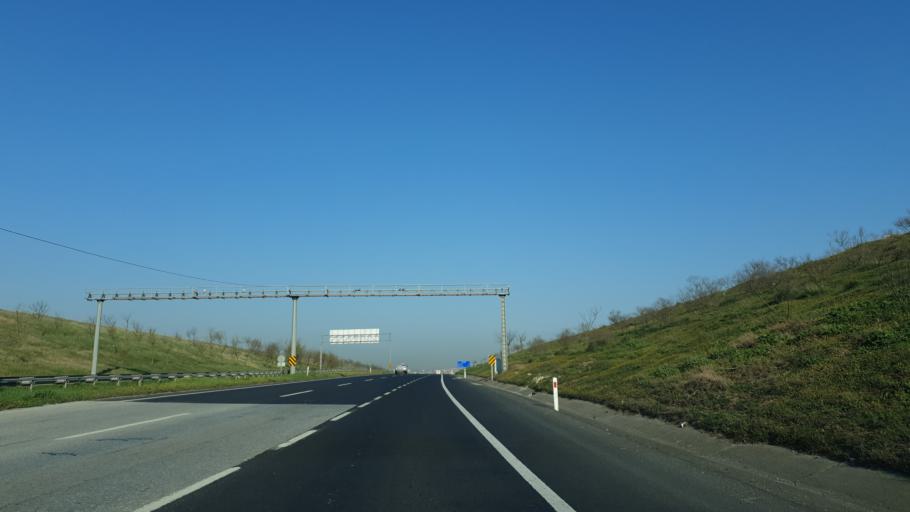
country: TR
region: Tekirdag
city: Corlu
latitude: 41.1799
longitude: 27.8065
